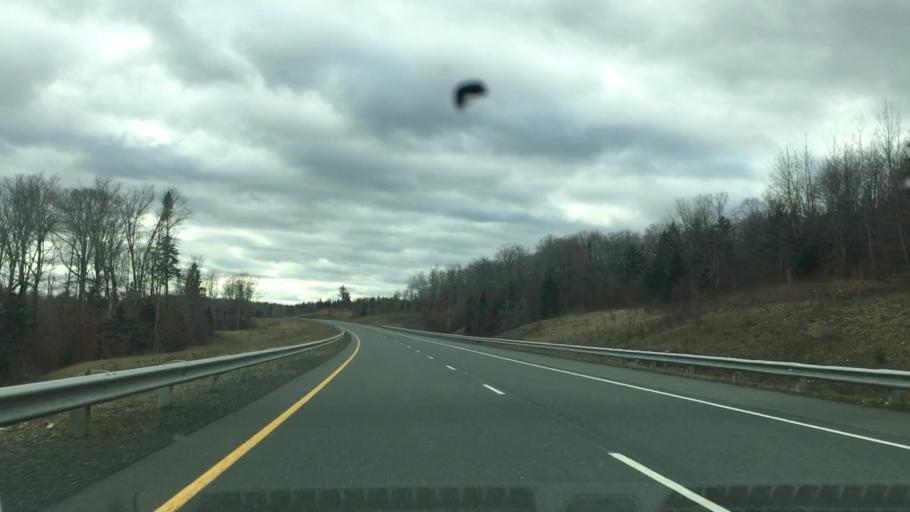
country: US
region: Maine
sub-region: Aroostook County
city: Fort Fairfield
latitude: 46.6468
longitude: -67.7432
